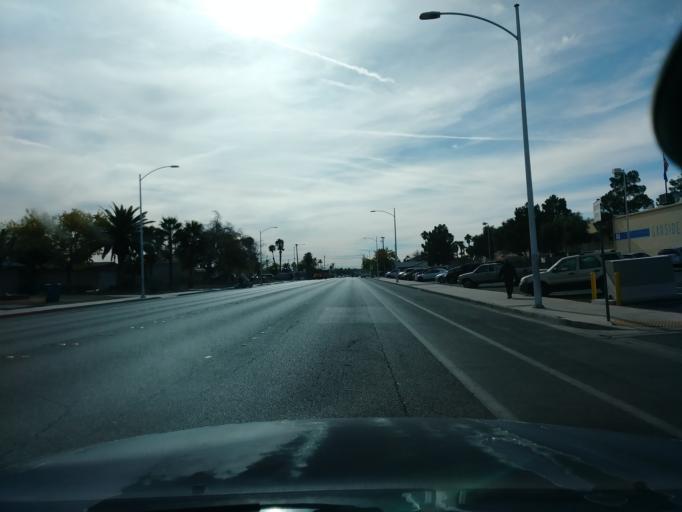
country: US
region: Nevada
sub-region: Clark County
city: Spring Valley
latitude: 36.1698
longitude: -115.2332
